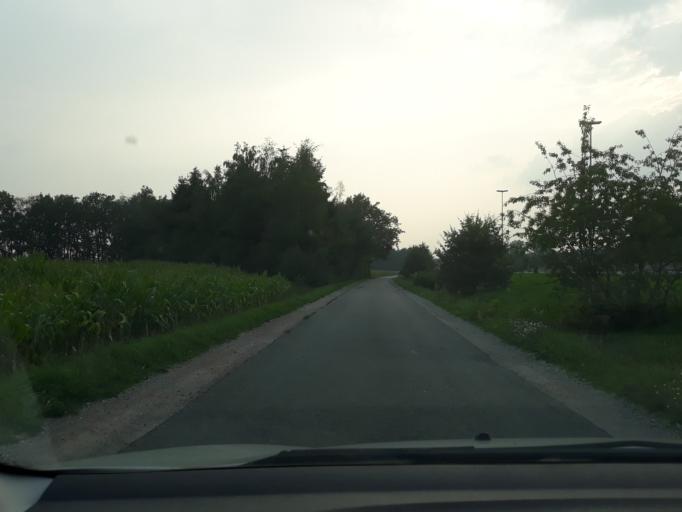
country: BE
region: Flanders
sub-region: Provincie Antwerpen
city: Lille
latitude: 51.2497
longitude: 4.7902
